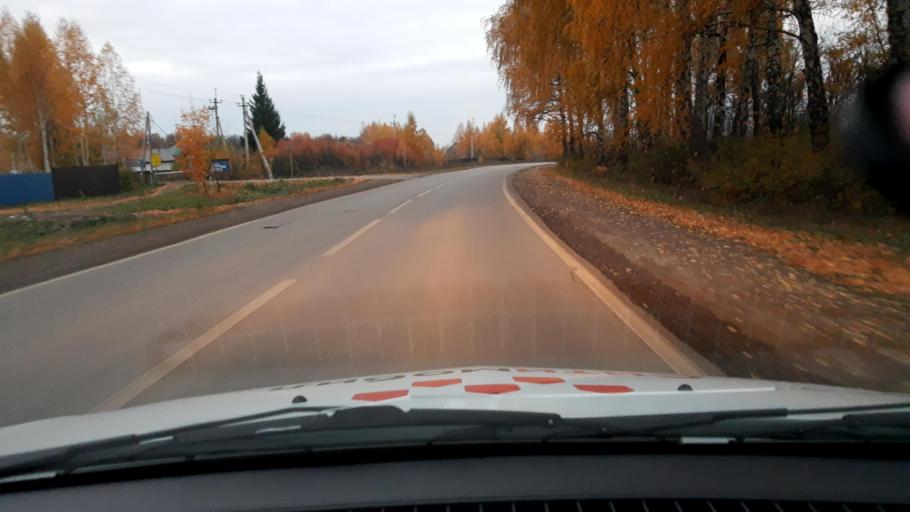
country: RU
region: Bashkortostan
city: Kabakovo
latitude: 54.7068
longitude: 56.1692
